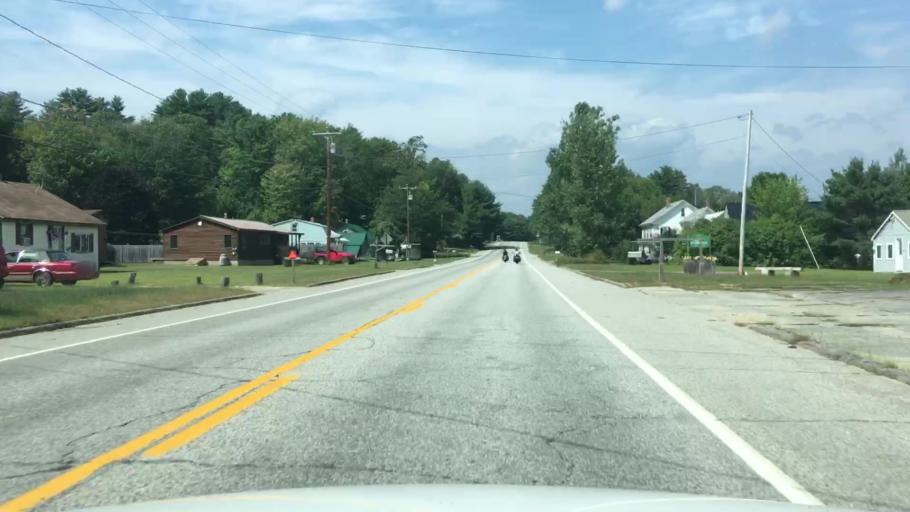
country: US
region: Maine
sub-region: Oxford County
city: Peru
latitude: 44.4880
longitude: -70.3791
